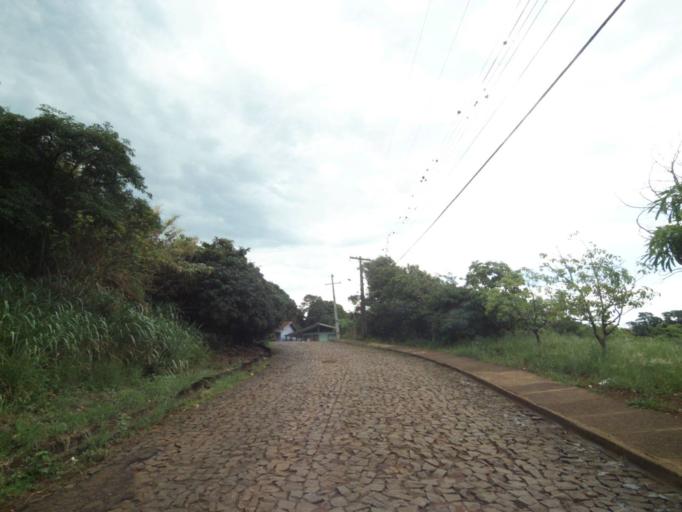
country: BR
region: Parana
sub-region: Guaraniacu
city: Guaraniacu
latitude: -25.0962
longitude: -52.8683
